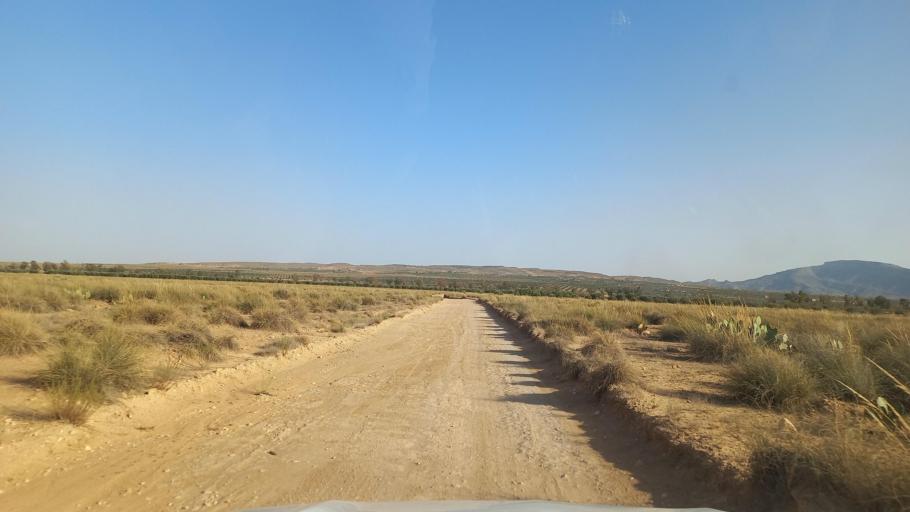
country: TN
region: Al Qasrayn
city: Kasserine
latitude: 35.2313
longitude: 8.9400
